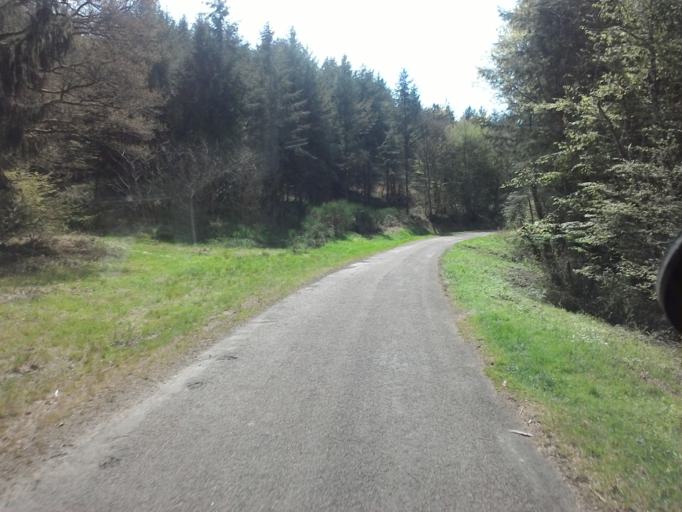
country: FR
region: Bourgogne
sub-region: Departement de la Nievre
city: Lormes
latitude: 47.3292
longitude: 3.9007
